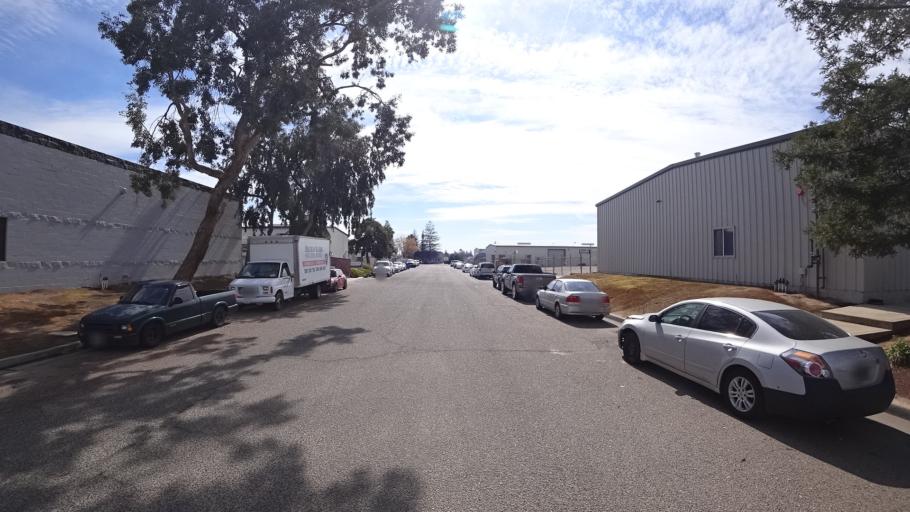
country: US
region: California
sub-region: Fresno County
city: West Park
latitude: 36.8145
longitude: -119.8902
